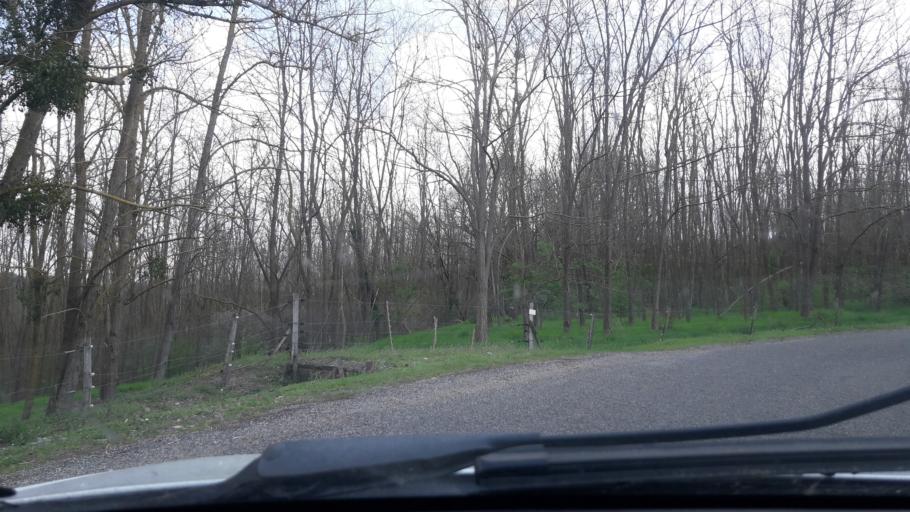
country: FR
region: Midi-Pyrenees
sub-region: Departement de la Haute-Garonne
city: Montesquieu-Volvestre
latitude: 43.2171
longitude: 1.2272
